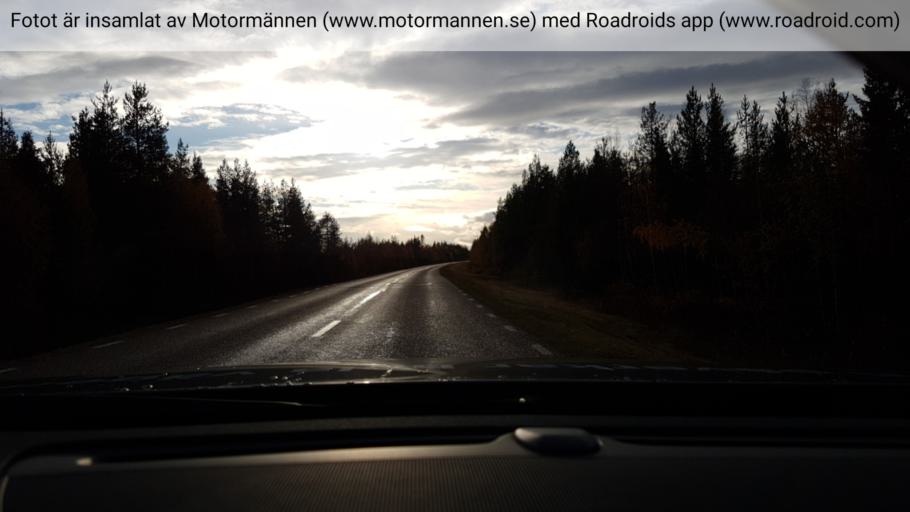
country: SE
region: Norrbotten
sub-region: Pajala Kommun
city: Pajala
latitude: 67.1695
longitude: 22.6729
